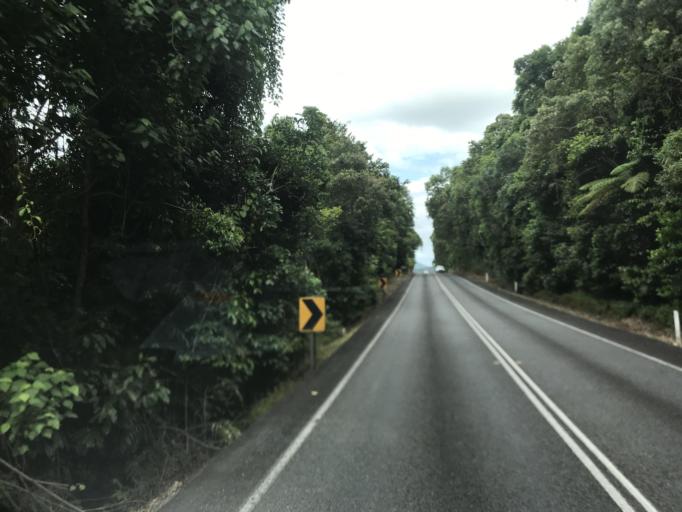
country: AU
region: Queensland
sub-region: Cassowary Coast
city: Innisfail
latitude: -17.8508
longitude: 146.0614
